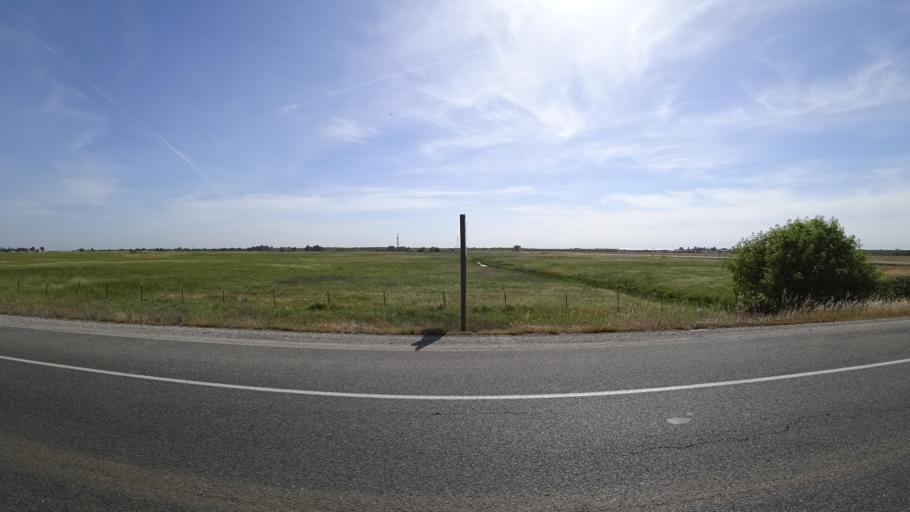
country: US
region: California
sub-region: Tehama County
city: Los Molinos
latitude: 39.9313
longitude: -122.0325
